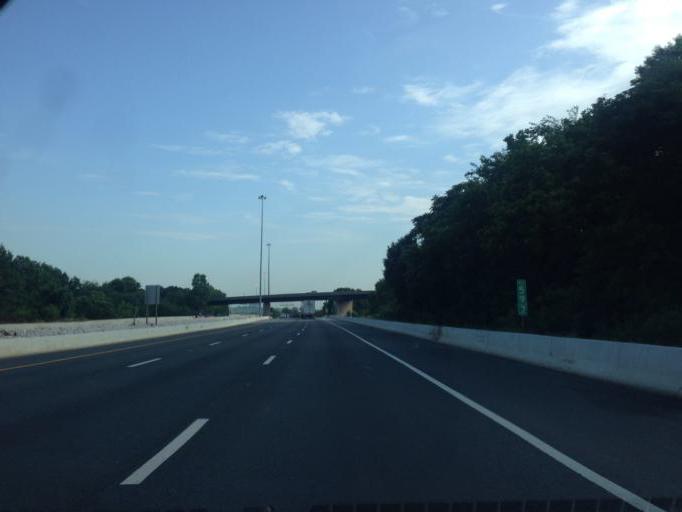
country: US
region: Maryland
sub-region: Baltimore County
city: Rosedale
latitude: 39.3036
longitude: -76.5304
